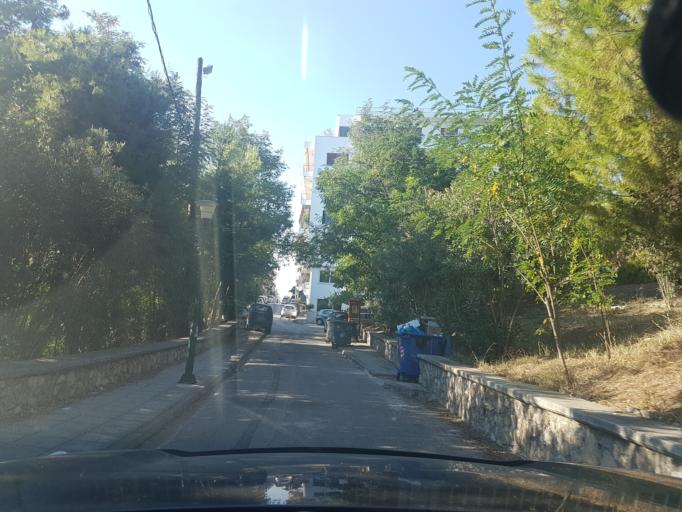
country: GR
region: Central Greece
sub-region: Nomos Evvoias
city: Chalkida
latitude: 38.4656
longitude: 23.5875
